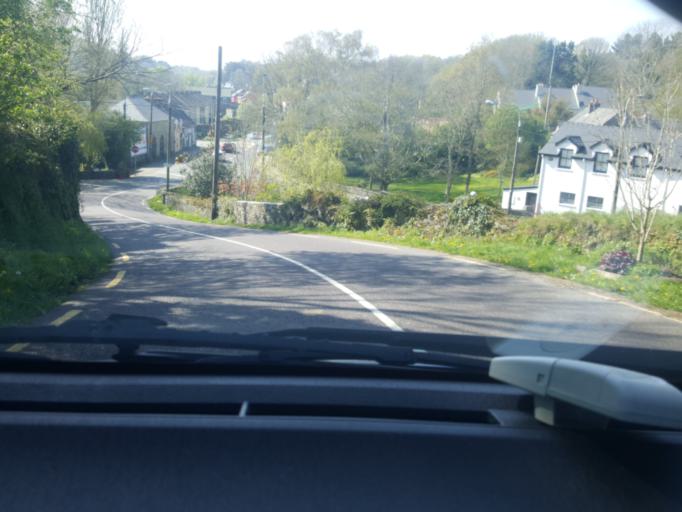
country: IE
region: Munster
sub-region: County Cork
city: Bandon
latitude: 51.7641
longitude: -8.6540
